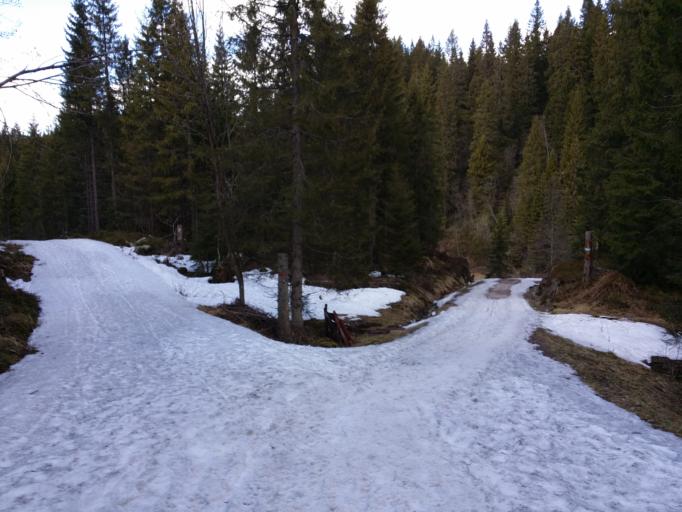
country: NO
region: Oslo
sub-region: Oslo
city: Sjolyststranda
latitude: 59.9878
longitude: 10.6879
